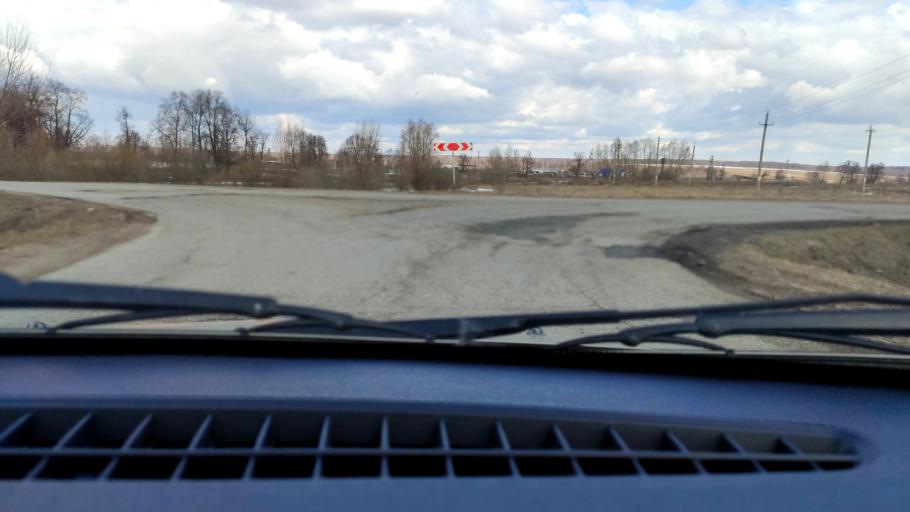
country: RU
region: Bashkortostan
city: Kudeyevskiy
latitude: 54.8507
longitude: 56.7955
